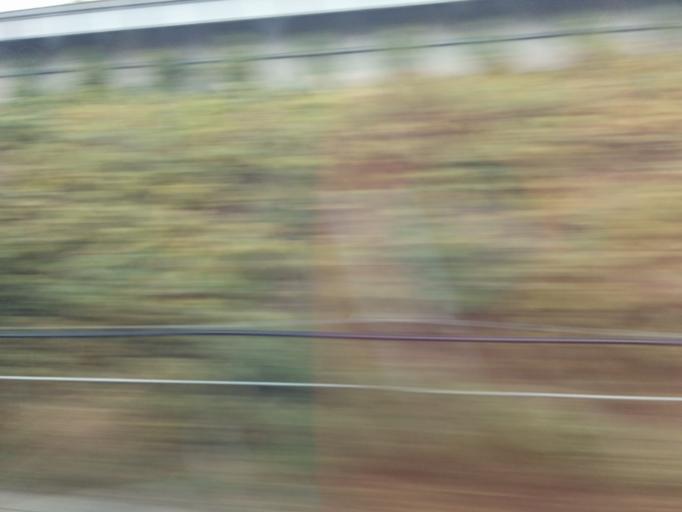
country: JP
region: Kanagawa
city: Minami-rinkan
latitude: 35.4239
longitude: 139.4463
